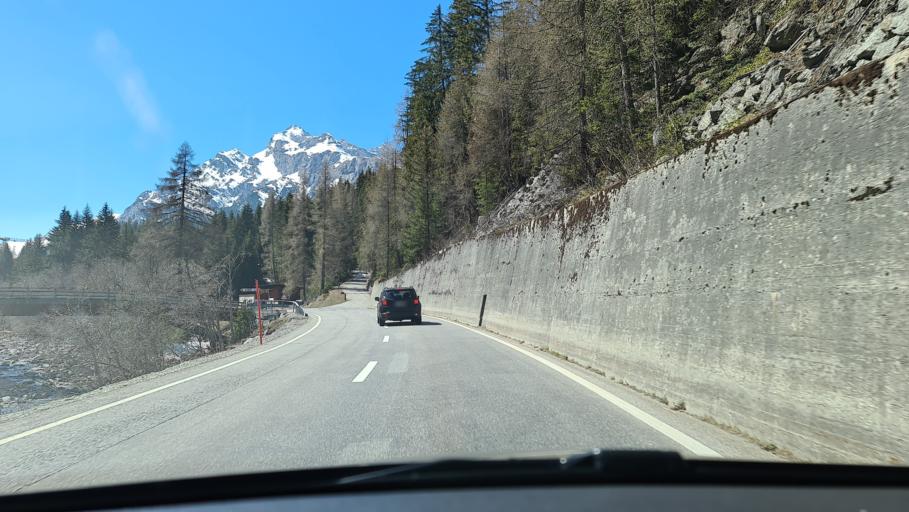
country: CH
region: Grisons
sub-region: Hinterrhein District
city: Thusis
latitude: 46.5688
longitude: 9.3920
